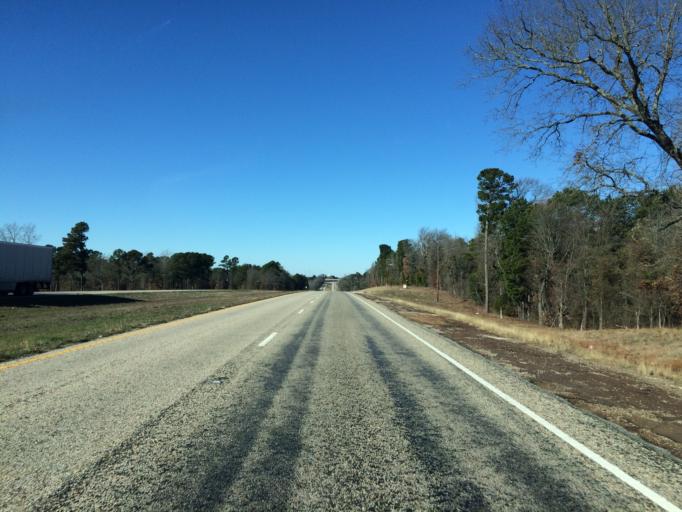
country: US
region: Texas
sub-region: Wood County
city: Mineola
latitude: 32.6534
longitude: -95.4451
